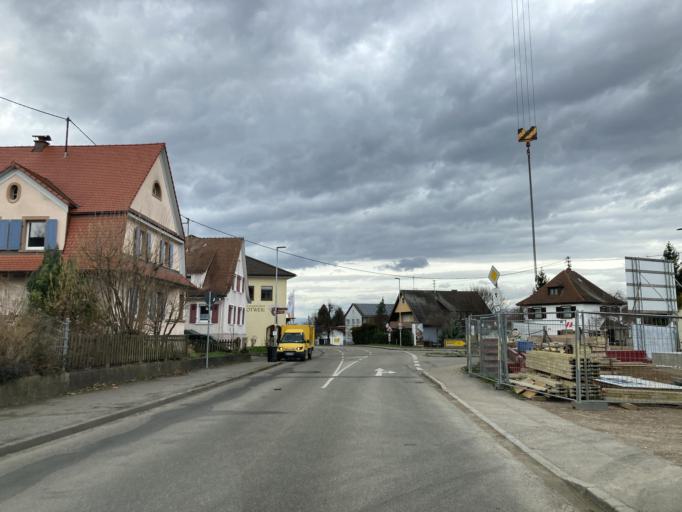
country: DE
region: Baden-Wuerttemberg
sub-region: Freiburg Region
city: Vogtsburg
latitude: 48.0902
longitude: 7.6254
